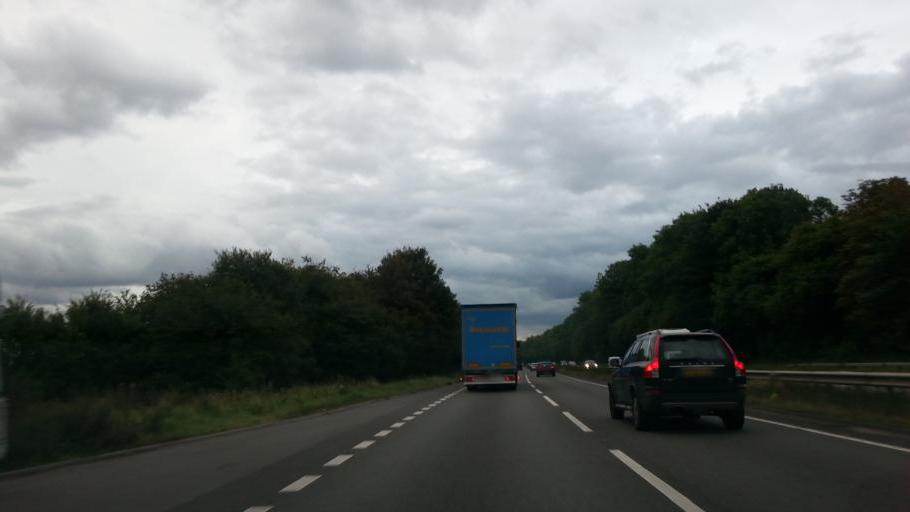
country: GB
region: England
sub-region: Nottinghamshire
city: Tuxford
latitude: 53.2412
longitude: -0.9013
